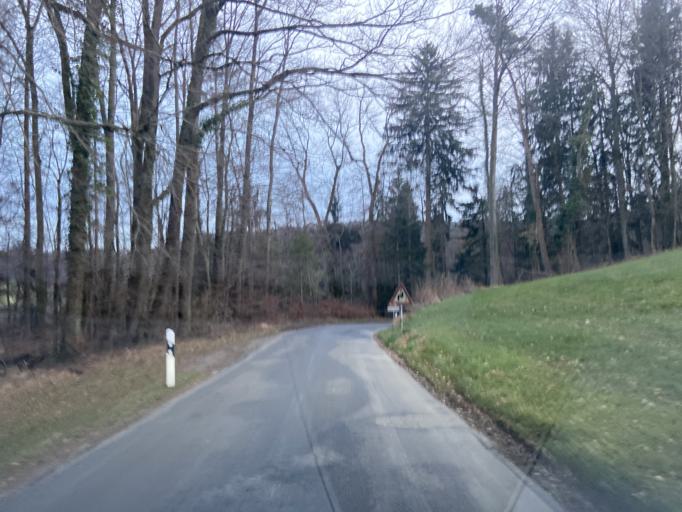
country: CH
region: Zurich
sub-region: Bezirk Winterthur
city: Wuelflingen (Kreis 6) / Niederfeld
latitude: 47.4959
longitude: 8.6683
